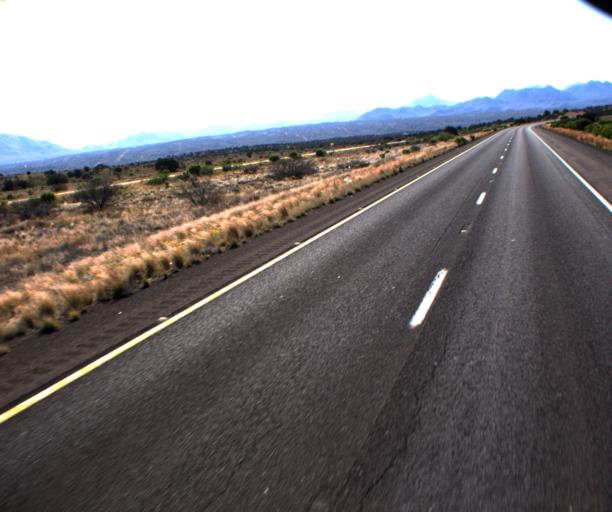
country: US
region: Arizona
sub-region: Mohave County
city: New Kingman-Butler
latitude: 35.1438
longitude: -113.6821
